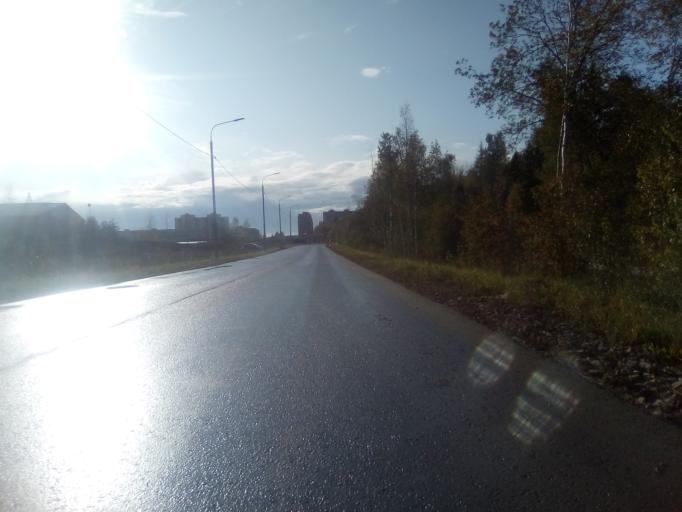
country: RU
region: Moskovskaya
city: Krasnoznamensk
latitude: 55.5837
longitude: 37.0531
